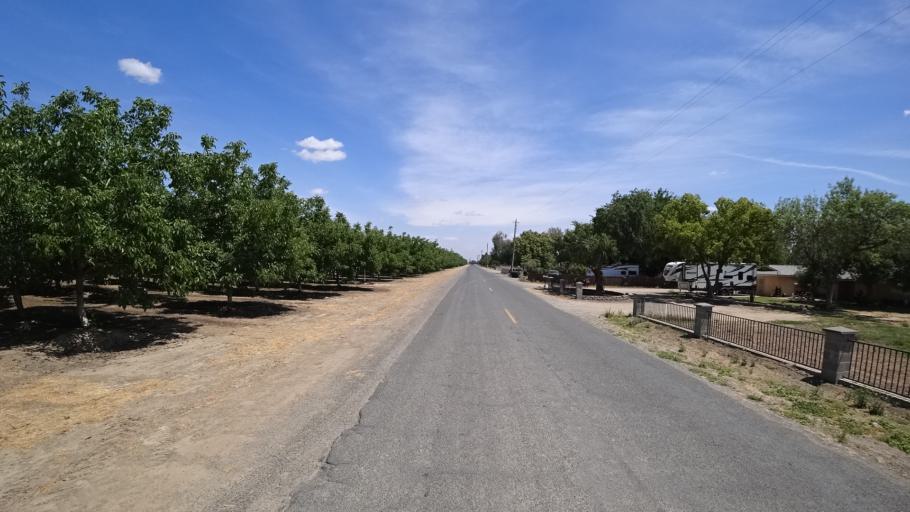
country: US
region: California
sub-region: Kings County
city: Home Garden
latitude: 36.2838
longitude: -119.6699
